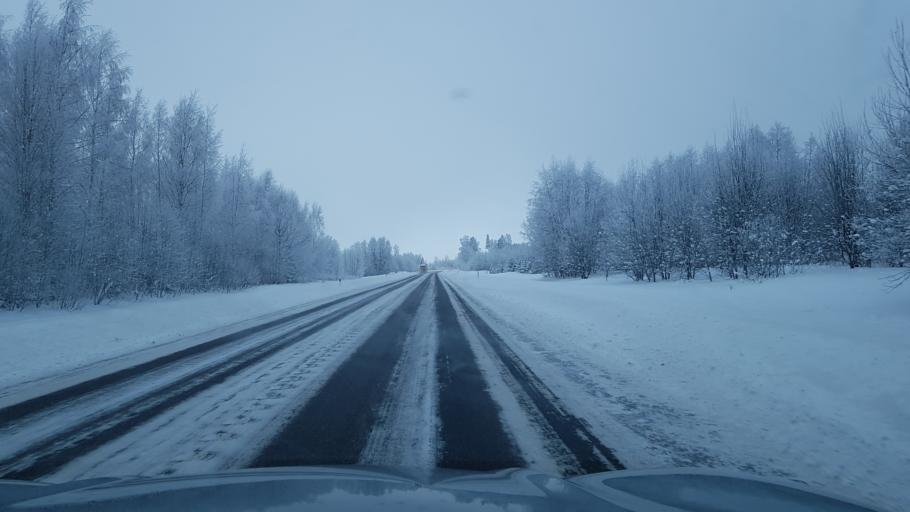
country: EE
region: Ida-Virumaa
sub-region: Johvi vald
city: Johvi
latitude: 59.2147
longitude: 27.3399
